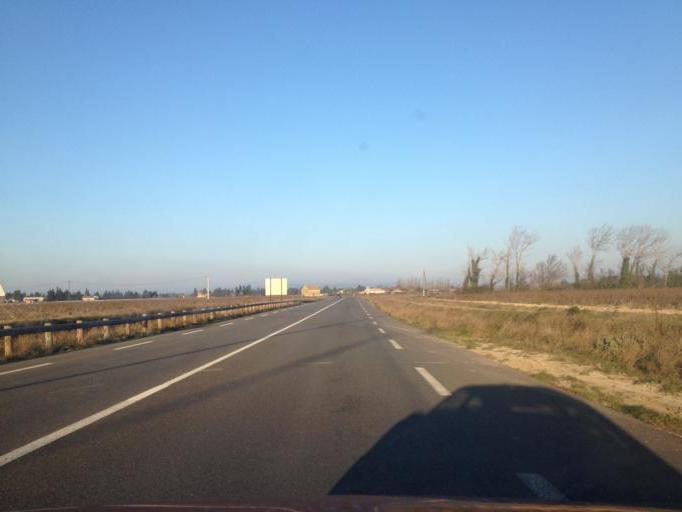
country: FR
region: Provence-Alpes-Cote d'Azur
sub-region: Departement du Vaucluse
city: Camaret-sur-Aigues
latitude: 44.1543
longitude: 4.8836
